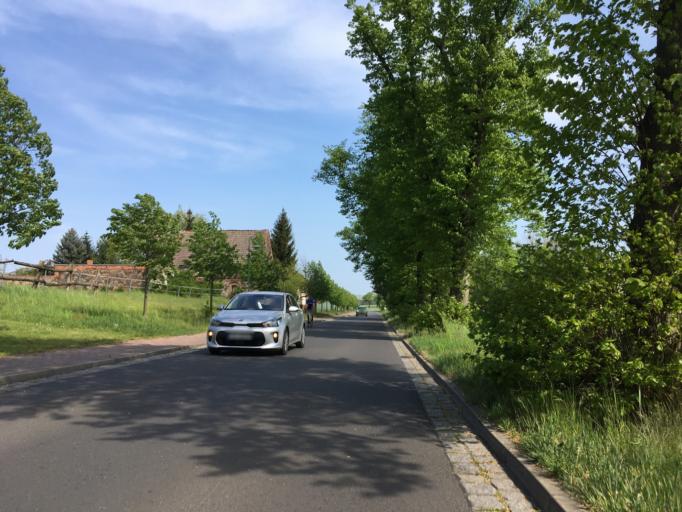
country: DE
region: Brandenburg
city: Werneuchen
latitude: 52.6044
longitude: 13.7563
